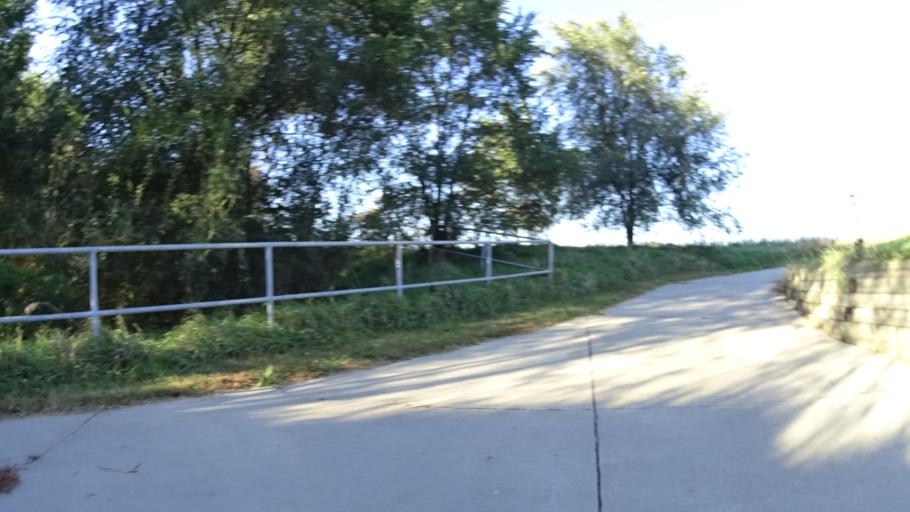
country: US
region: Nebraska
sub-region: Sarpy County
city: Papillion
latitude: 41.1470
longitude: -96.0675
